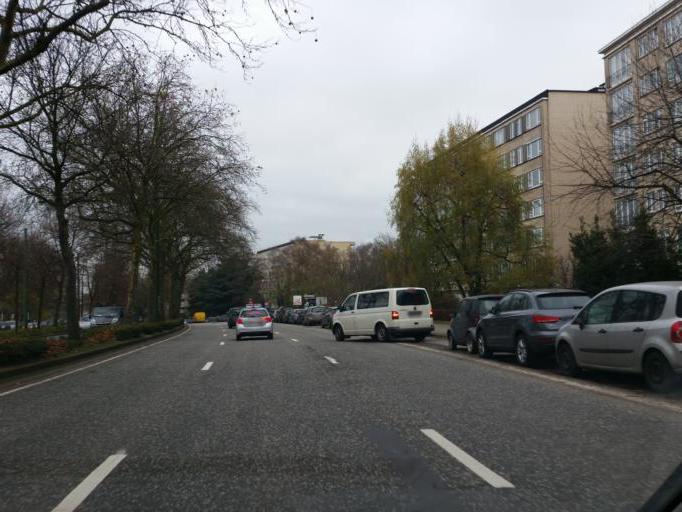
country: BE
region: Brussels Capital
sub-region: Bruxelles-Capitale
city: Brussels
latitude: 50.8590
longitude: 4.3958
